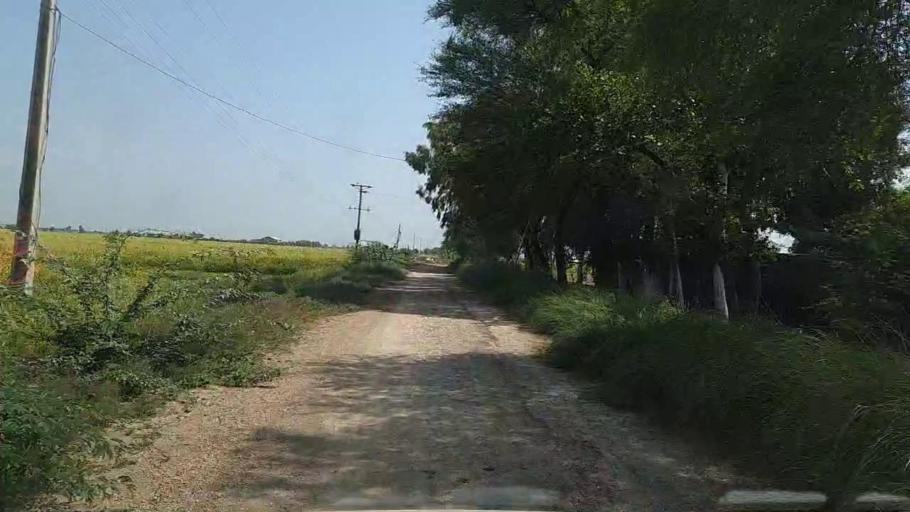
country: PK
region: Sindh
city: Kario
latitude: 24.6346
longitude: 68.5395
